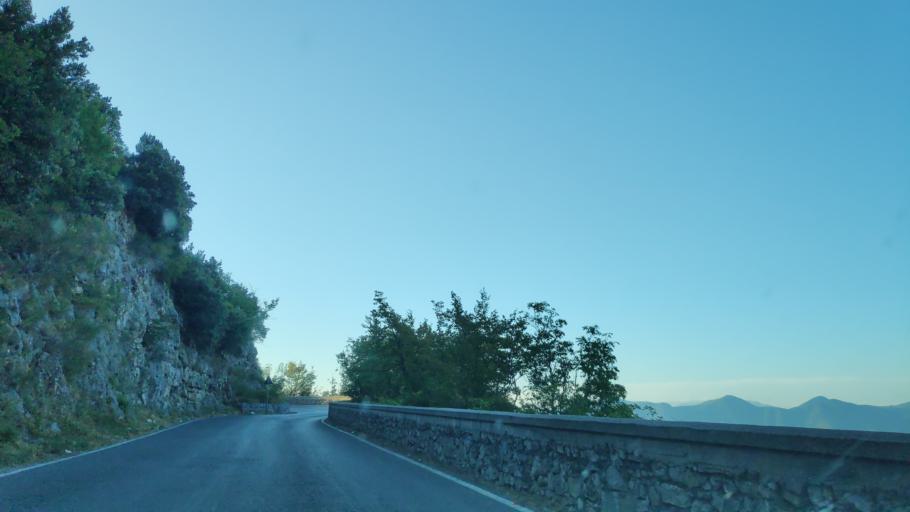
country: IT
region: Campania
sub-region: Provincia di Salerno
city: Corbara
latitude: 40.7239
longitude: 14.6060
